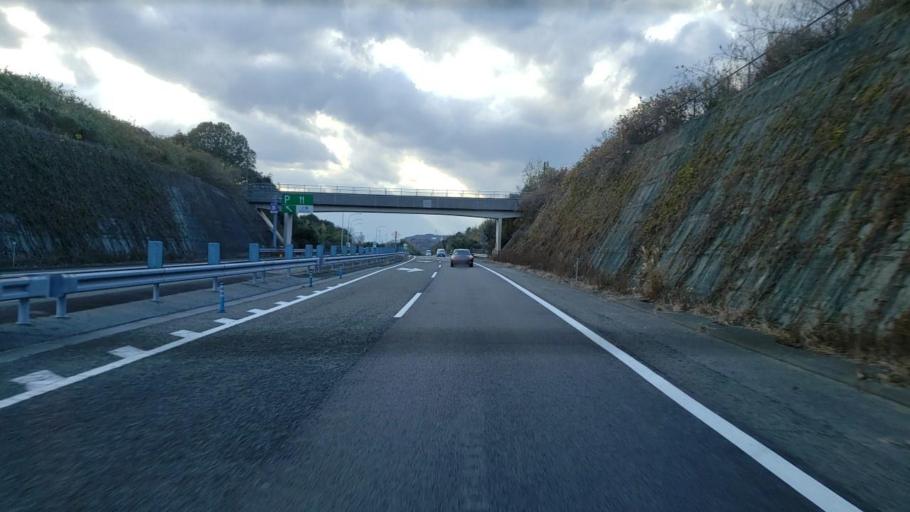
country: JP
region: Tokushima
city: Ishii
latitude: 34.1424
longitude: 134.4215
